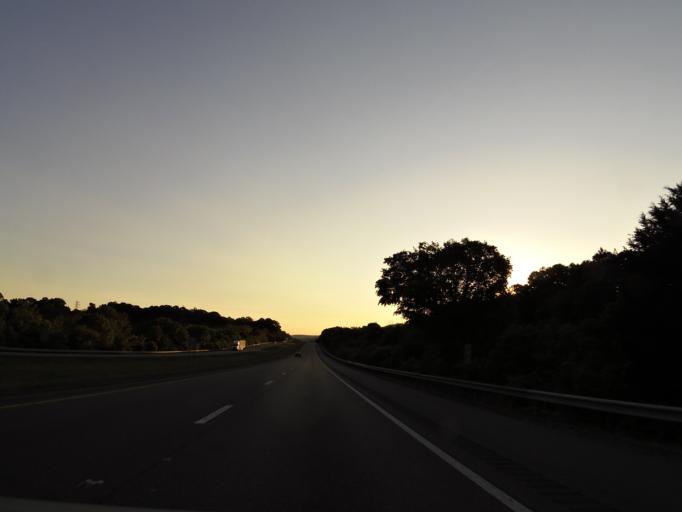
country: US
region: Tennessee
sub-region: Washington County
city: Fall Branch
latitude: 36.3560
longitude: -82.7230
